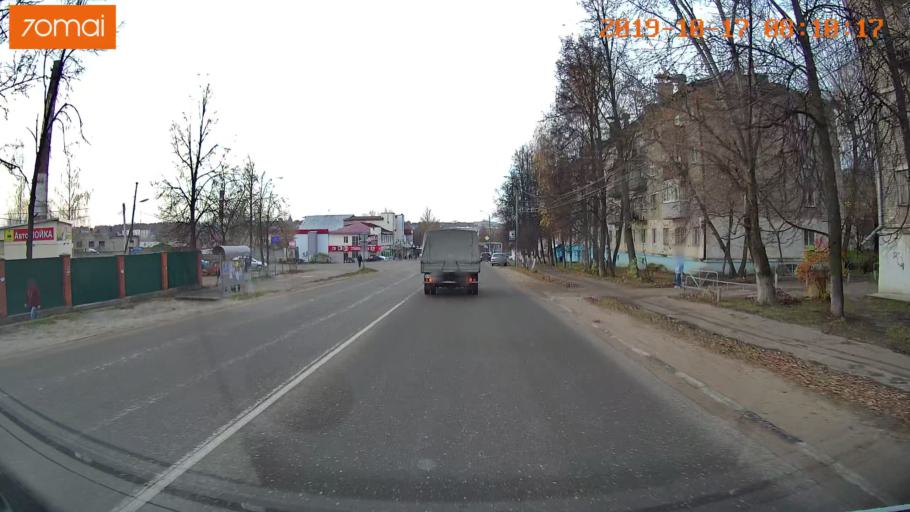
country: RU
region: Vladimir
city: Kol'chugino
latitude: 56.3084
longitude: 39.3780
